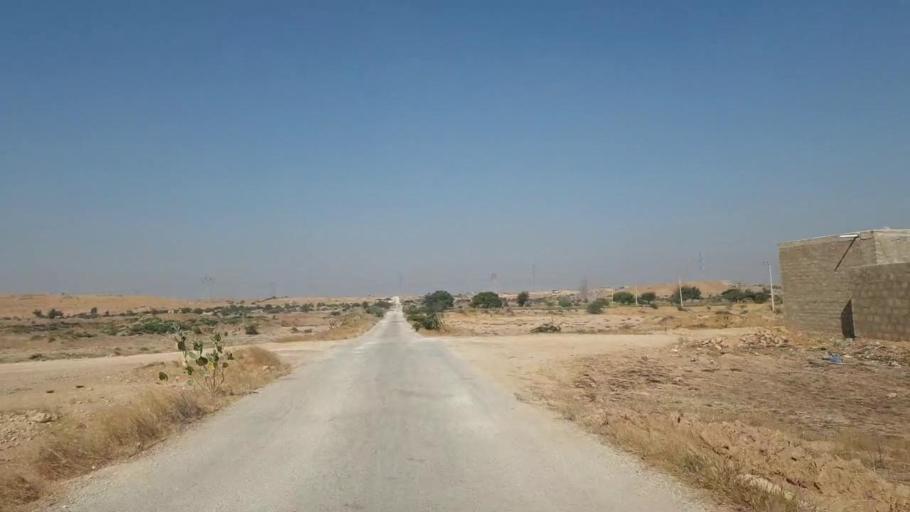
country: PK
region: Sindh
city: Thatta
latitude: 25.1904
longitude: 67.8031
